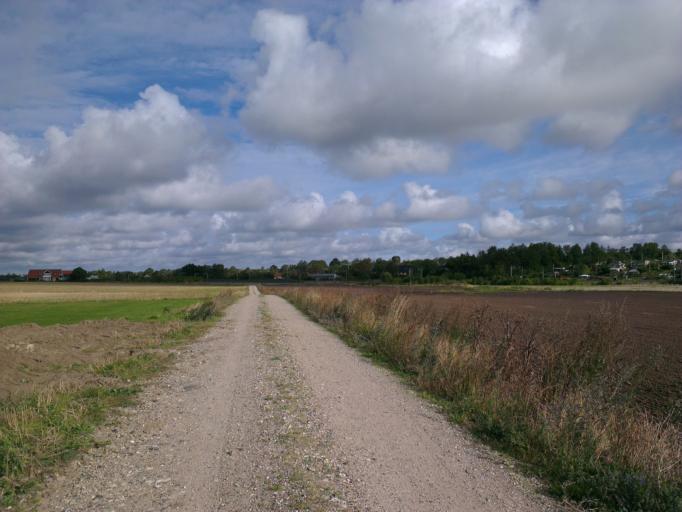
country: DK
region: Capital Region
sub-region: Frederikssund Kommune
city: Frederikssund
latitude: 55.8150
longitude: 12.0869
